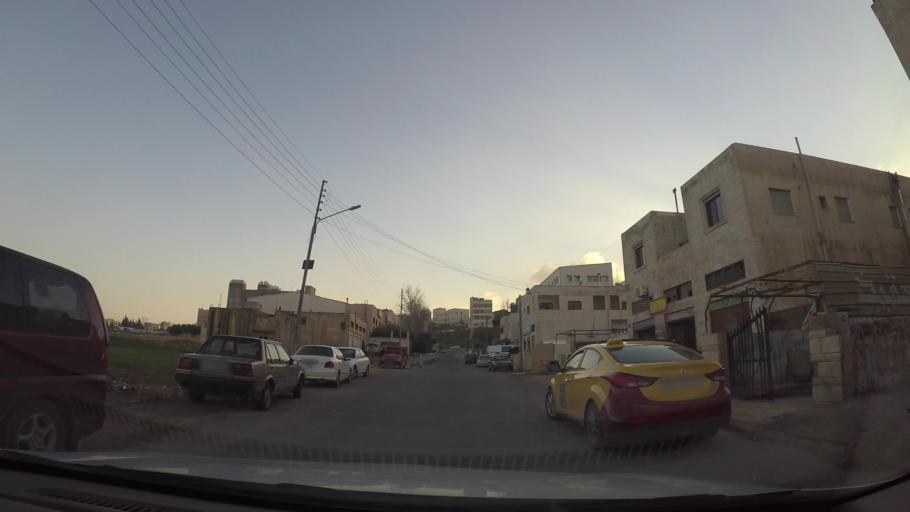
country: JO
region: Amman
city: Al Bunayyat ash Shamaliyah
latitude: 31.9077
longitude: 35.9198
